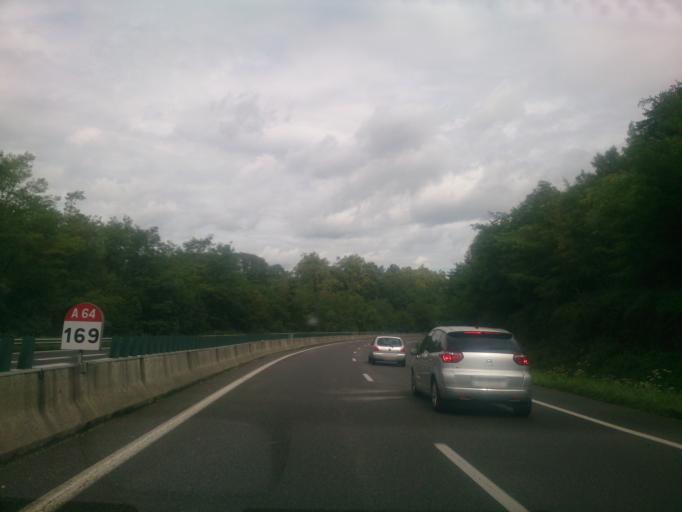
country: FR
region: Midi-Pyrenees
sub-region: Departement des Hautes-Pyrenees
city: Capvern
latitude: 43.1091
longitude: 0.3219
